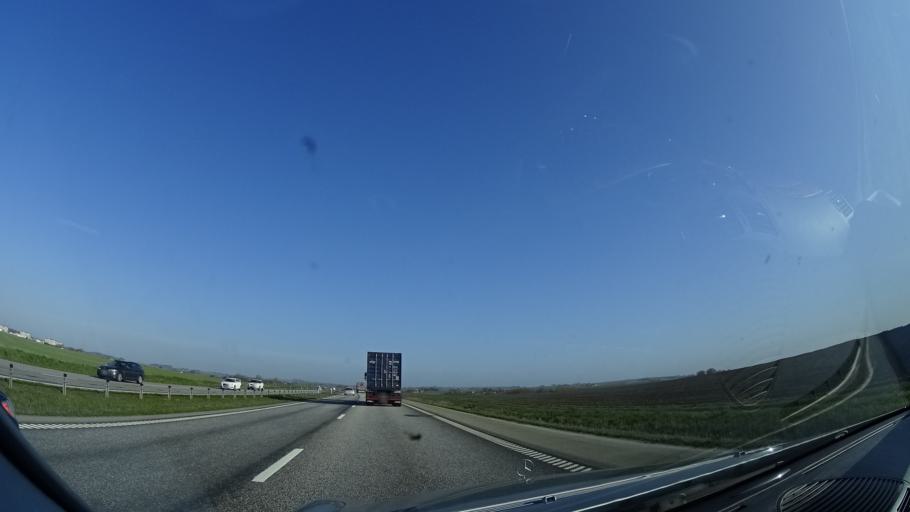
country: SE
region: Skane
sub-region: Landskrona
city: Landskrona
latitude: 55.8848
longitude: 12.8762
